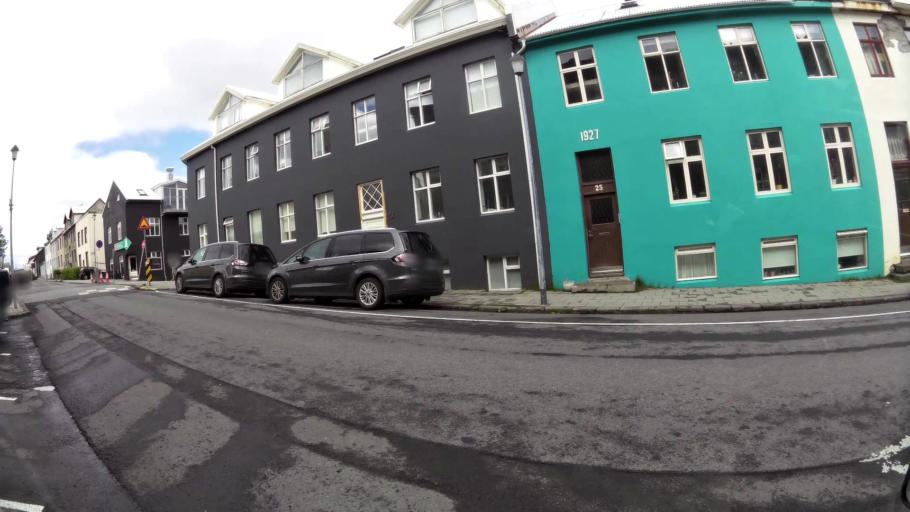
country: IS
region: Capital Region
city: Reykjavik
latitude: 64.1425
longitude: -21.9228
